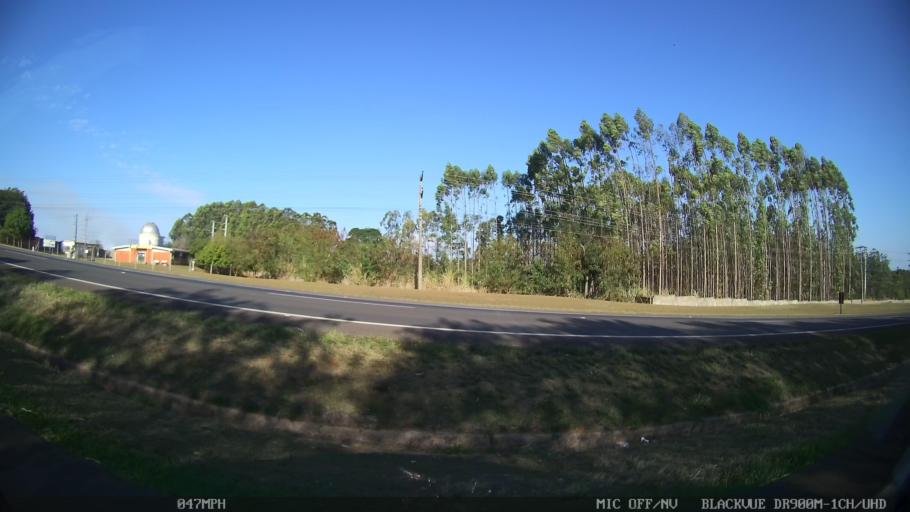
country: BR
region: Sao Paulo
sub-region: Piracicaba
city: Piracicaba
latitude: -22.6914
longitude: -47.6457
